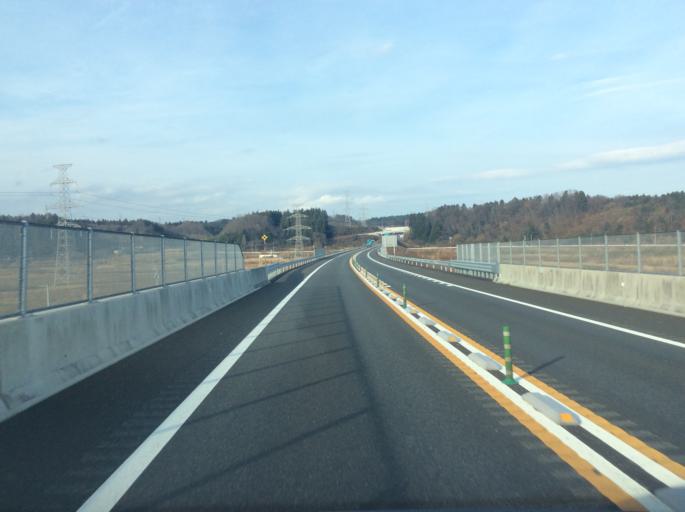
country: JP
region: Fukushima
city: Namie
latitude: 37.5041
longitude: 140.9422
